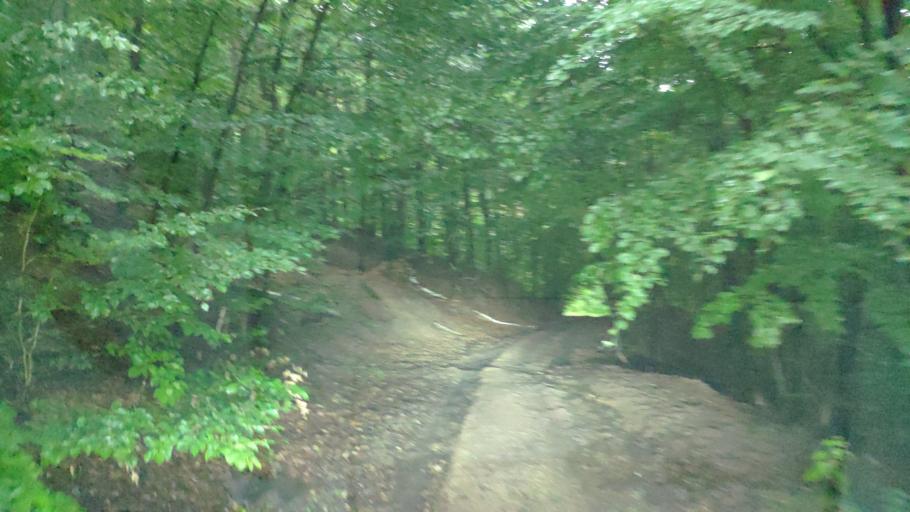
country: SK
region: Presovsky
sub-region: Okres Presov
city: Presov
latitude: 48.8696
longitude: 21.2086
